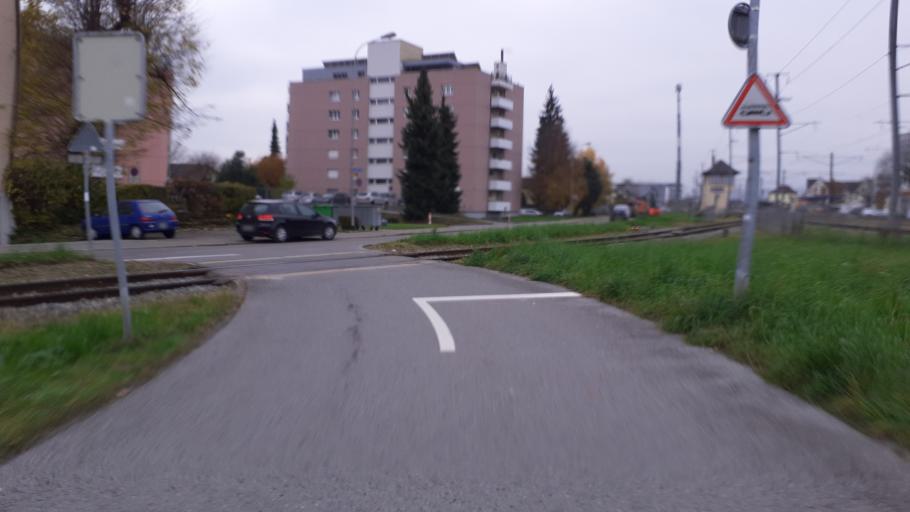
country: CH
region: Saint Gallen
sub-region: Wahlkreis Rheintal
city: Au
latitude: 47.4125
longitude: 9.6307
